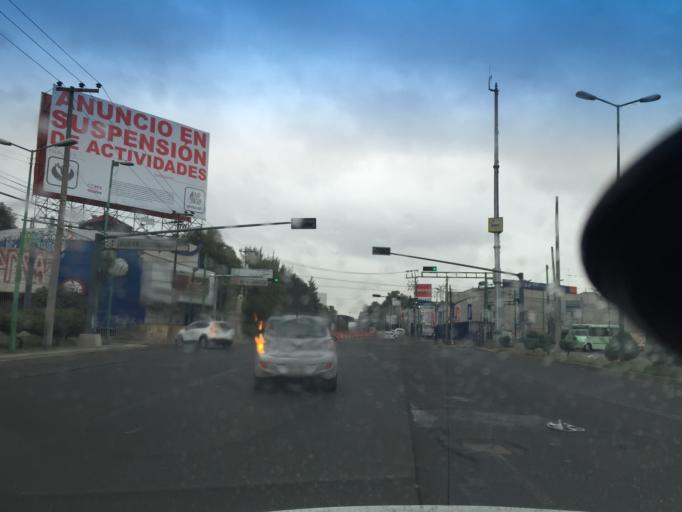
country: MX
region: Mexico
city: Colonia Lindavista
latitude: 19.4935
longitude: -99.1463
